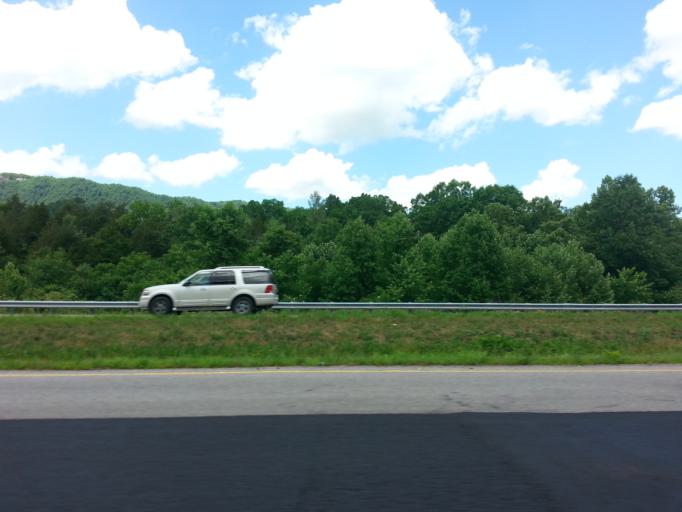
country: US
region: Kentucky
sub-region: Harlan County
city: Harlan
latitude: 36.6918
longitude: -83.2911
